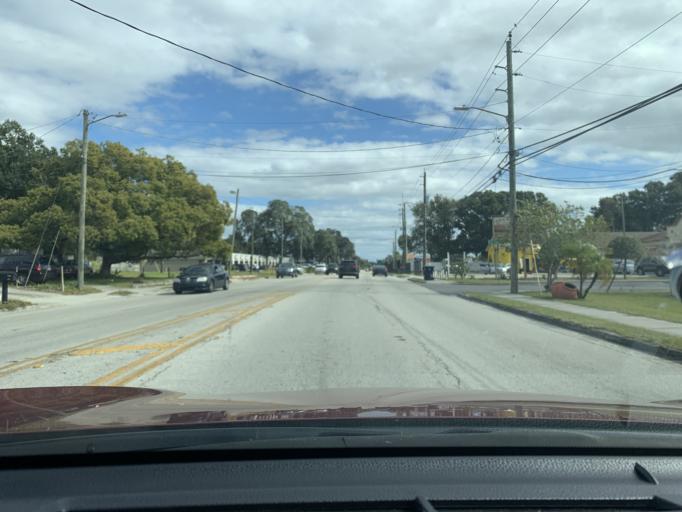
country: US
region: Florida
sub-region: Hillsborough County
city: Tampa
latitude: 27.9667
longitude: -82.4962
